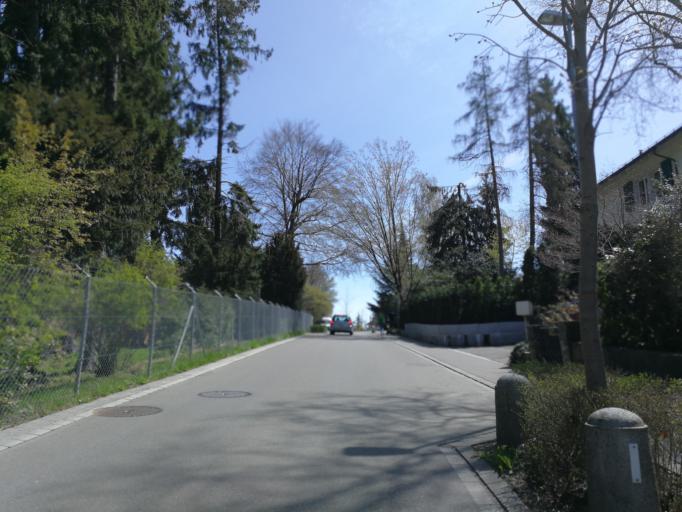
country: CH
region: Zurich
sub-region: Bezirk Meilen
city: Feldmeilen
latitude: 47.2824
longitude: 8.6222
